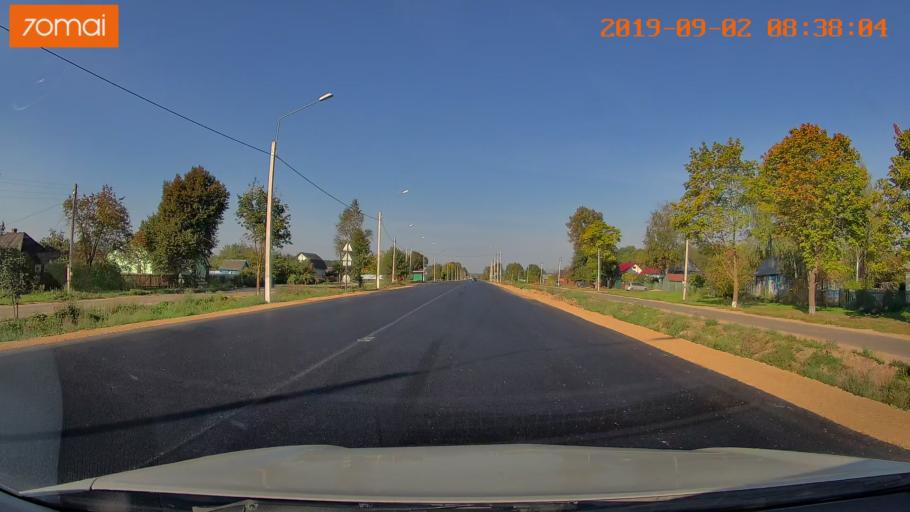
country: RU
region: Kaluga
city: Kudinovo
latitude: 54.9783
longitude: 36.1862
